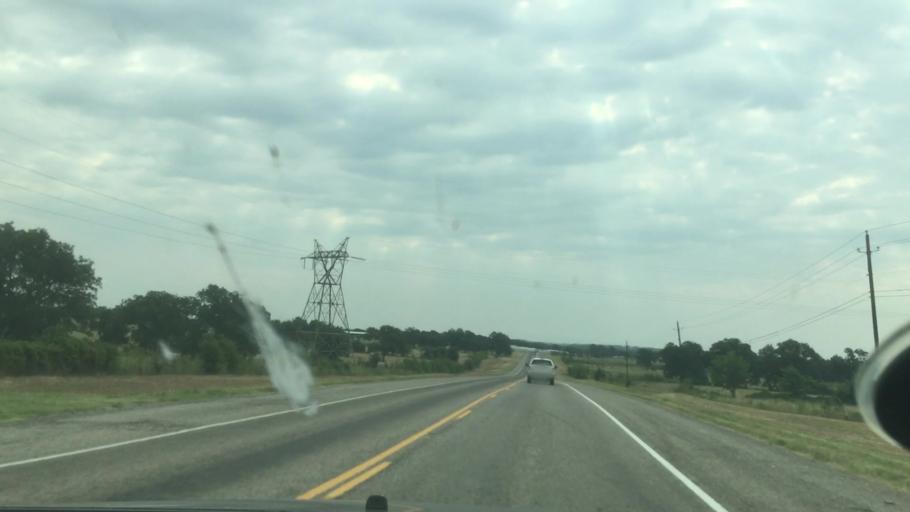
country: US
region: Texas
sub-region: Grayson County
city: Pottsboro
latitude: 33.7965
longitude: -96.6251
